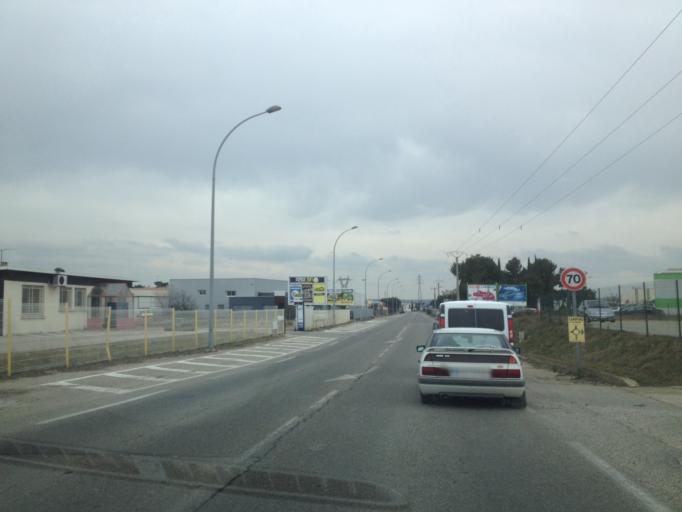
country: FR
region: Provence-Alpes-Cote d'Azur
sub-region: Departement du Vaucluse
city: Sorgues
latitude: 44.0109
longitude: 4.8872
